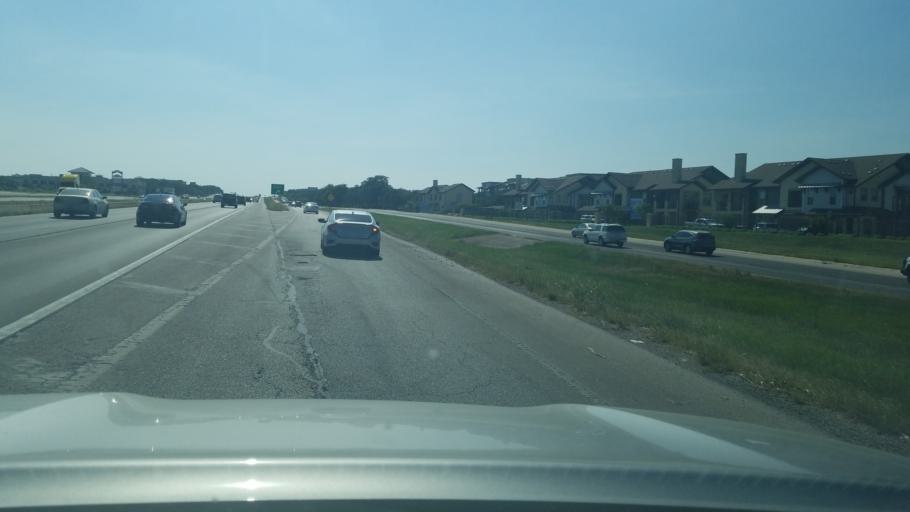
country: US
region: Texas
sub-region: Bexar County
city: Shavano Park
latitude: 29.6030
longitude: -98.5435
